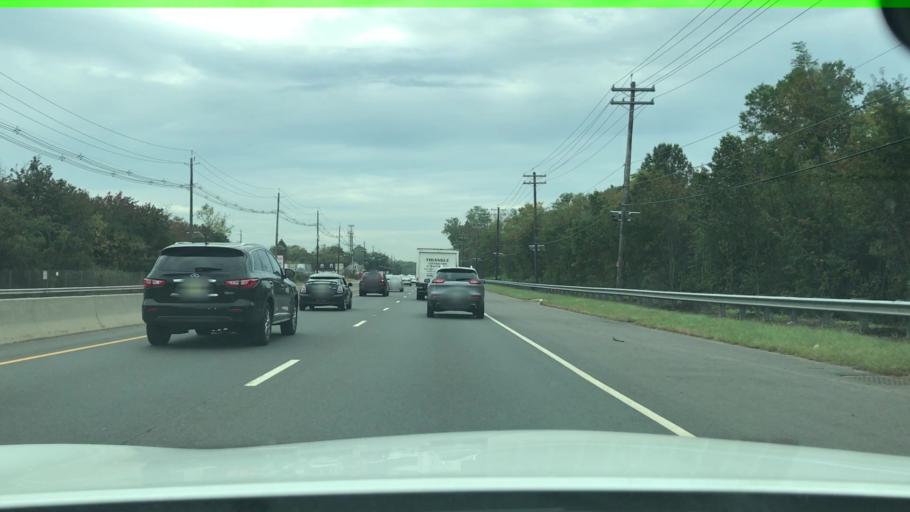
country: US
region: New Jersey
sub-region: Somerset County
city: Raritan
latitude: 40.5644
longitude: -74.6223
